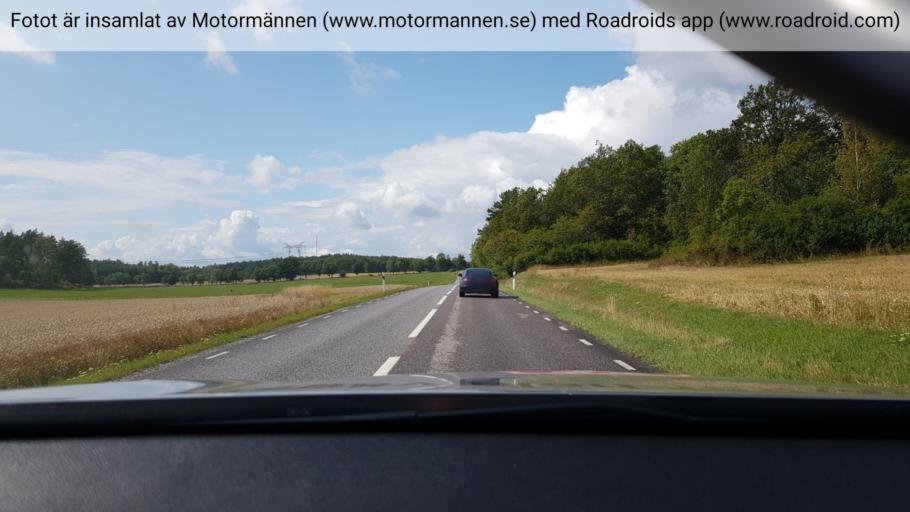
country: SE
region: Stockholm
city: Stenhamra
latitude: 59.2973
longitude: 17.6667
